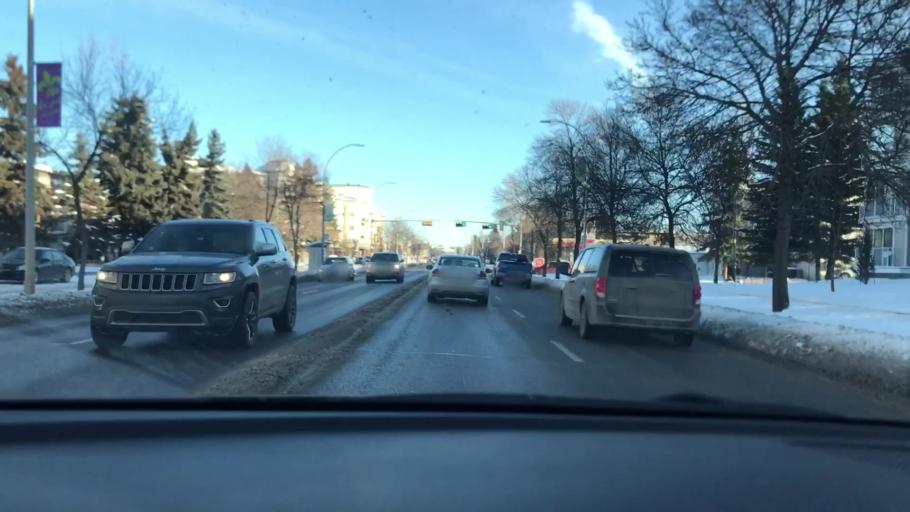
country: CA
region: Alberta
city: Edmonton
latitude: 53.5180
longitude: -113.4628
